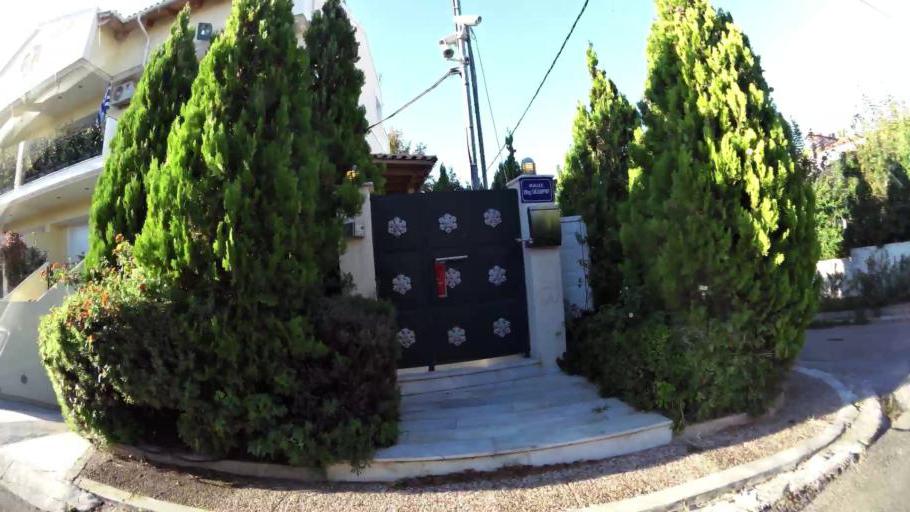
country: GR
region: Attica
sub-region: Nomarchia Athinas
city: Agia Paraskevi
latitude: 38.0260
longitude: 23.8403
